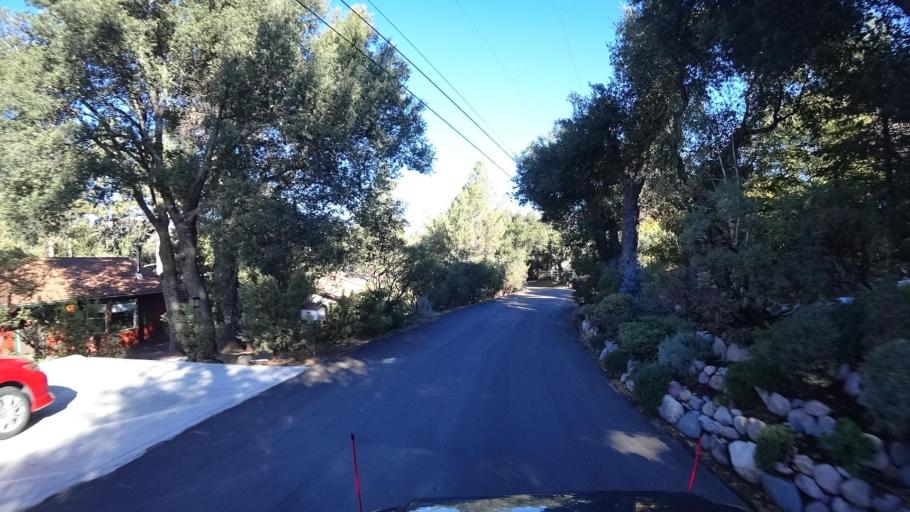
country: US
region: California
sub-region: San Diego County
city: Pine Valley
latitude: 32.8316
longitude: -116.5255
